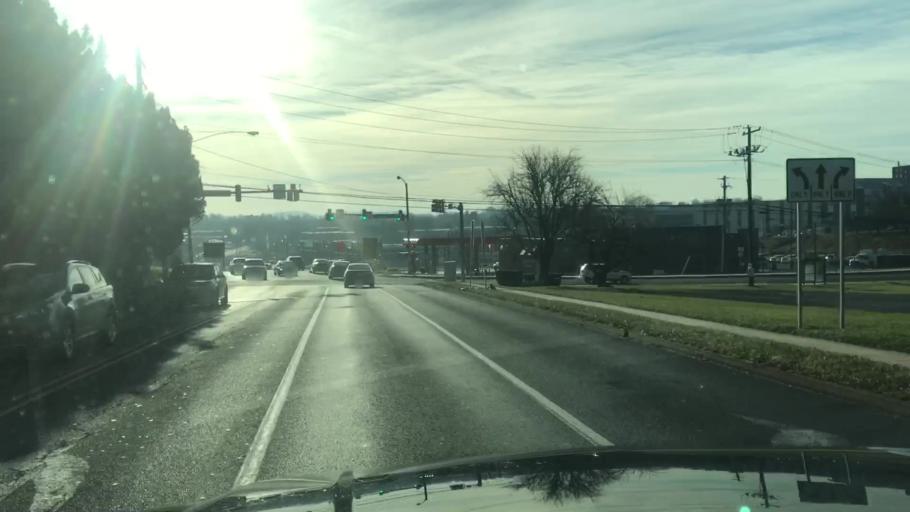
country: US
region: Pennsylvania
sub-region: Cumberland County
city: Wormleysburg
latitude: 40.2595
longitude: -76.9184
